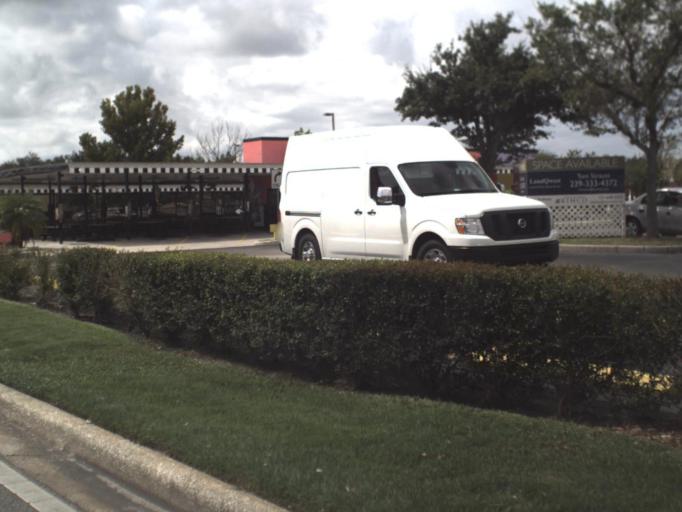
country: US
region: Florida
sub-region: Manatee County
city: Bayshore Gardens
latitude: 27.4342
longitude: -82.5756
